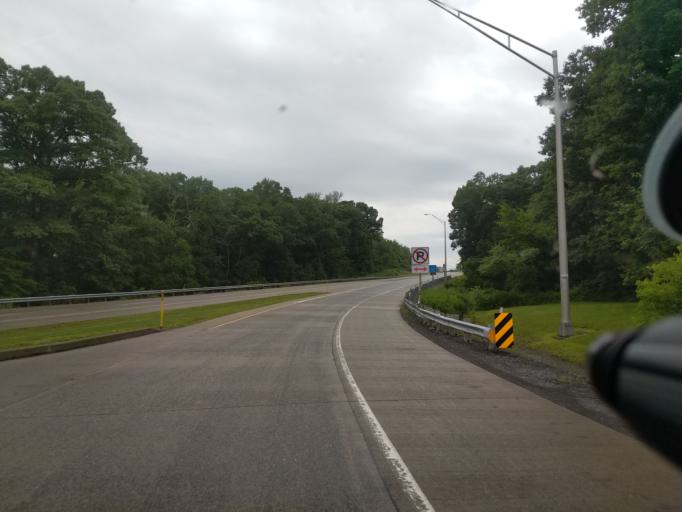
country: US
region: Pennsylvania
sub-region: Northumberland County
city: Riverside
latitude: 40.9908
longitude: -76.7274
